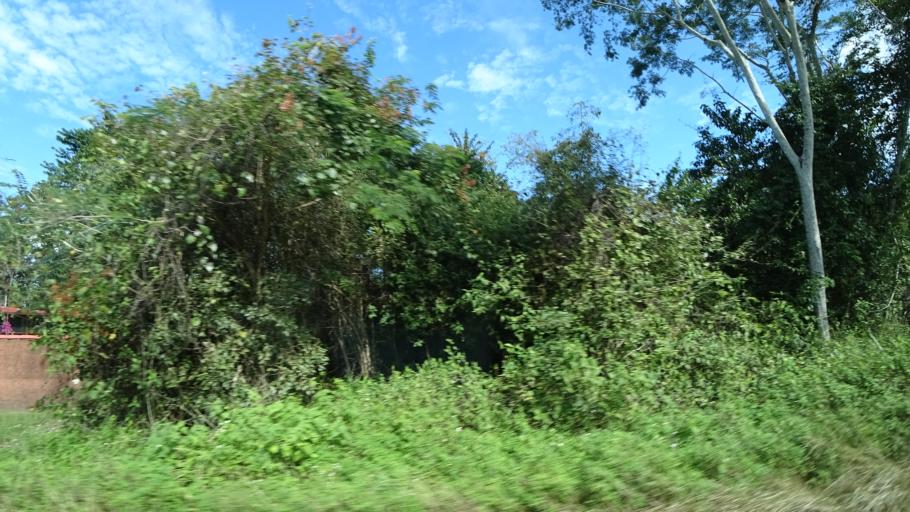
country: BZ
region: Belize
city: Belize City
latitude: 17.5717
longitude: -88.3929
